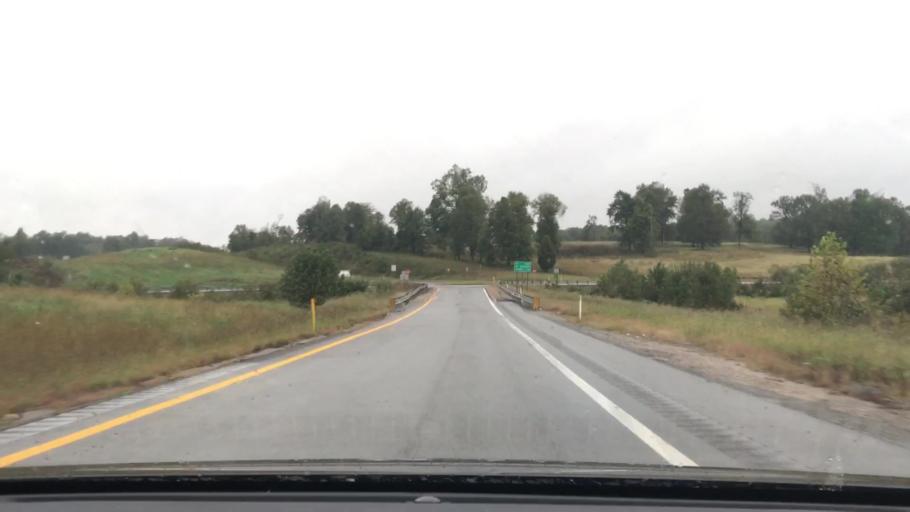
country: US
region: Kentucky
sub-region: Webster County
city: Sebree
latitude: 37.4887
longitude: -87.4746
